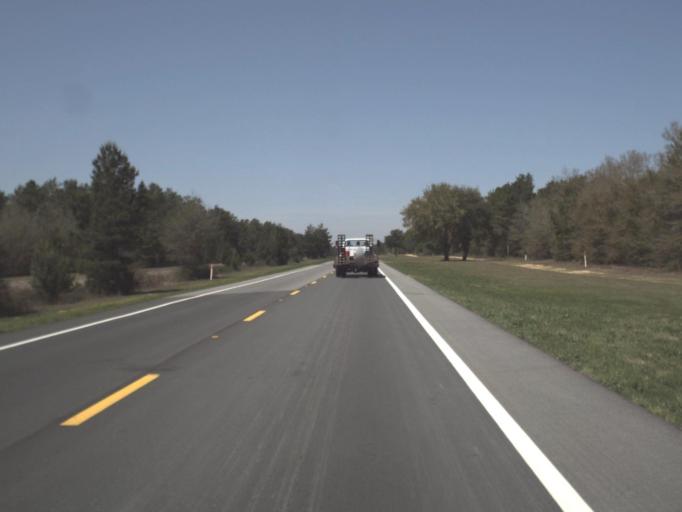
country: US
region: Florida
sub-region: Okaloosa County
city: Crestview
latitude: 30.7385
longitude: -86.3656
